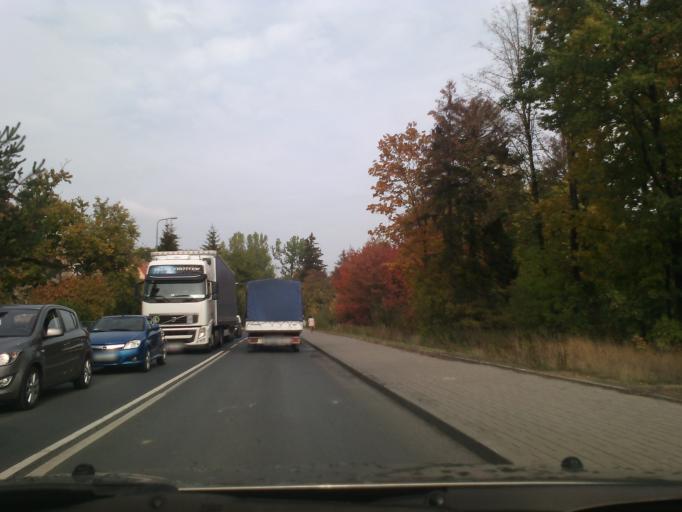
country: PL
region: Lower Silesian Voivodeship
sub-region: Jelenia Gora
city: Cieplice Slaskie Zdroj
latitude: 50.8710
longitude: 15.6842
